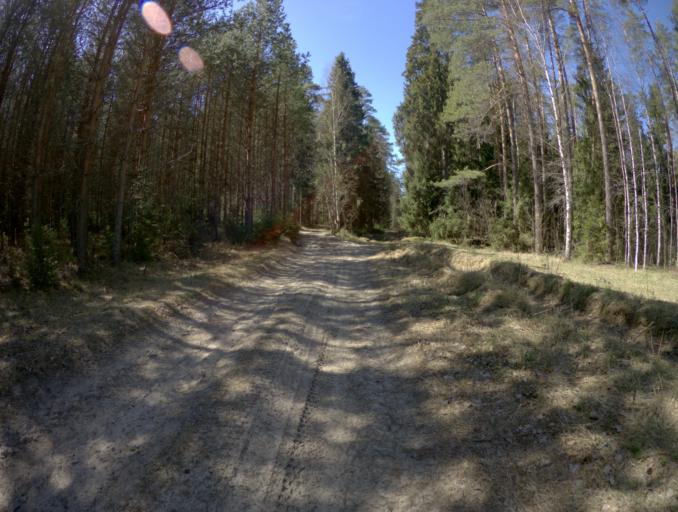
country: RU
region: Vladimir
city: Golovino
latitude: 55.9008
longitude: 40.4352
